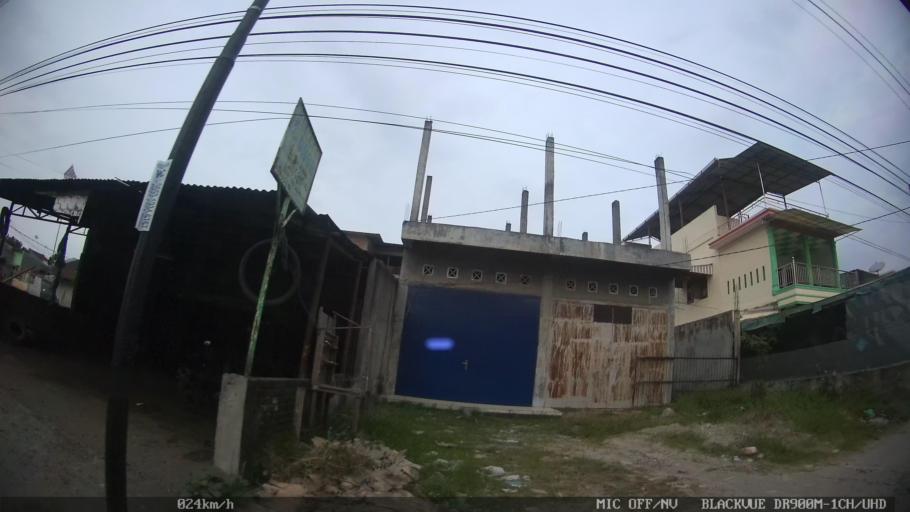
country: ID
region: North Sumatra
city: Sunggal
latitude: 3.5660
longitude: 98.6041
